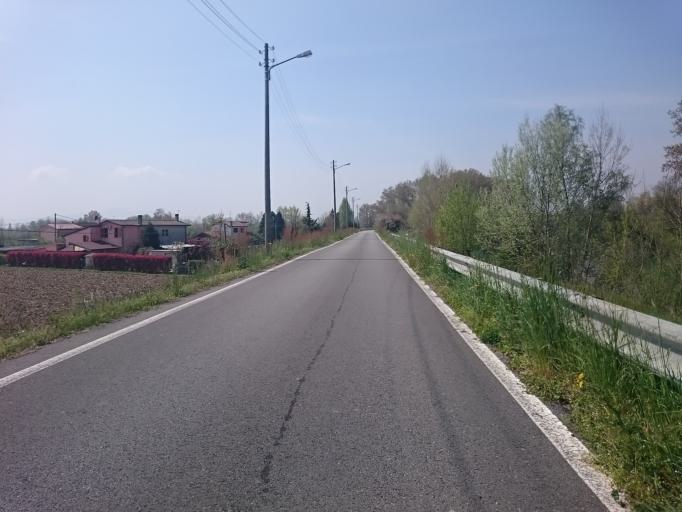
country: IT
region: Veneto
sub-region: Provincia di Padova
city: Tencarola
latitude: 45.3871
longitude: 11.8210
